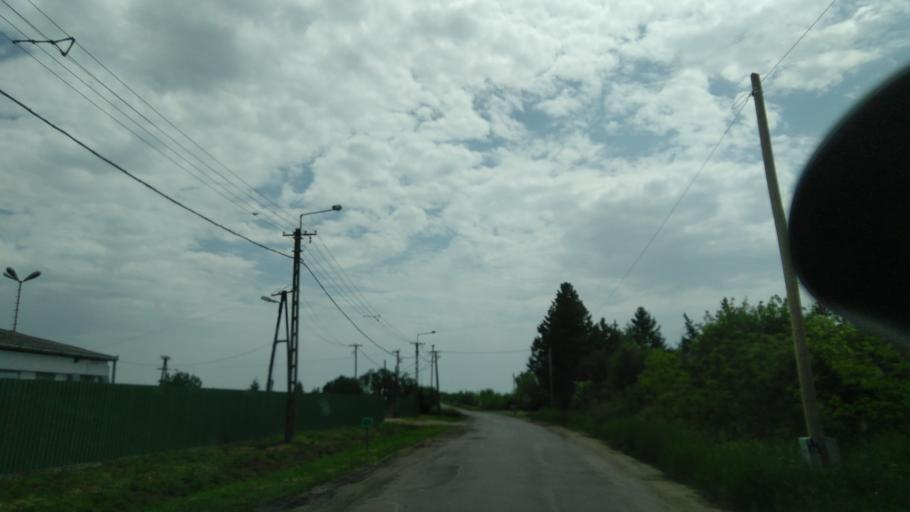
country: HU
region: Hajdu-Bihar
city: Komadi
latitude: 47.0147
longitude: 21.6021
